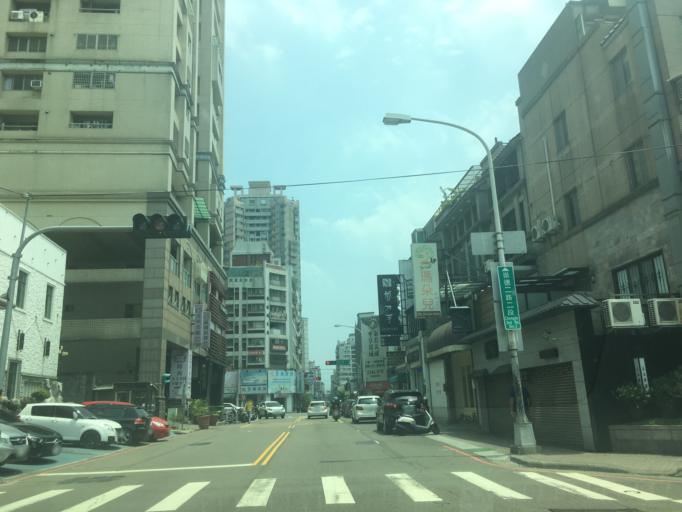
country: TW
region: Taiwan
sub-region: Taichung City
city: Taichung
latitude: 24.1776
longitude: 120.6850
